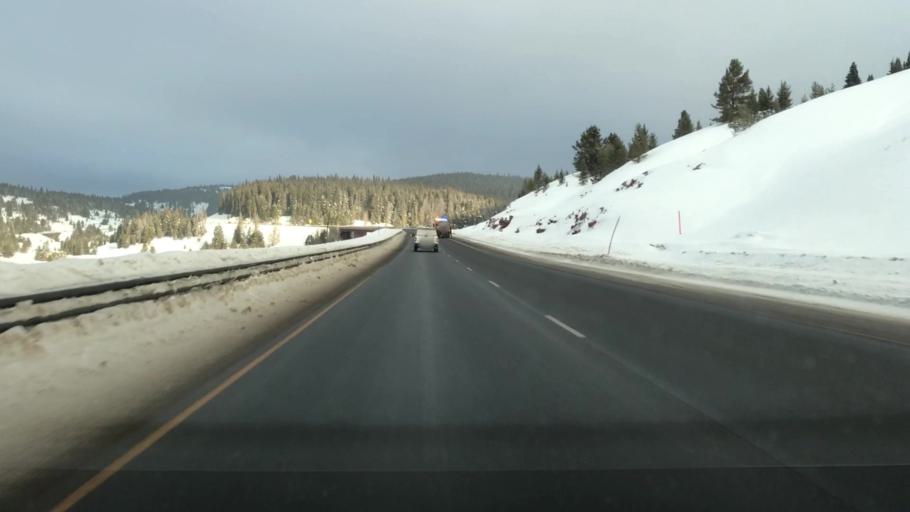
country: US
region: Colorado
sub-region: Summit County
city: Frisco
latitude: 39.5123
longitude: -106.2038
